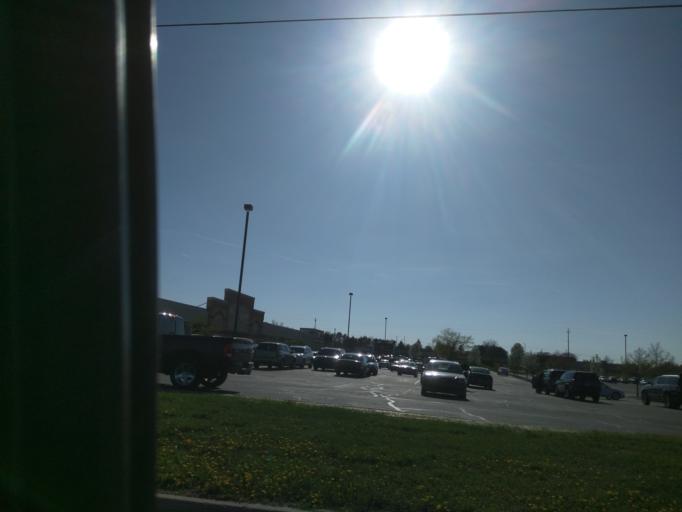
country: US
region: Michigan
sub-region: Eaton County
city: Waverly
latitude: 42.7394
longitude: -84.6298
